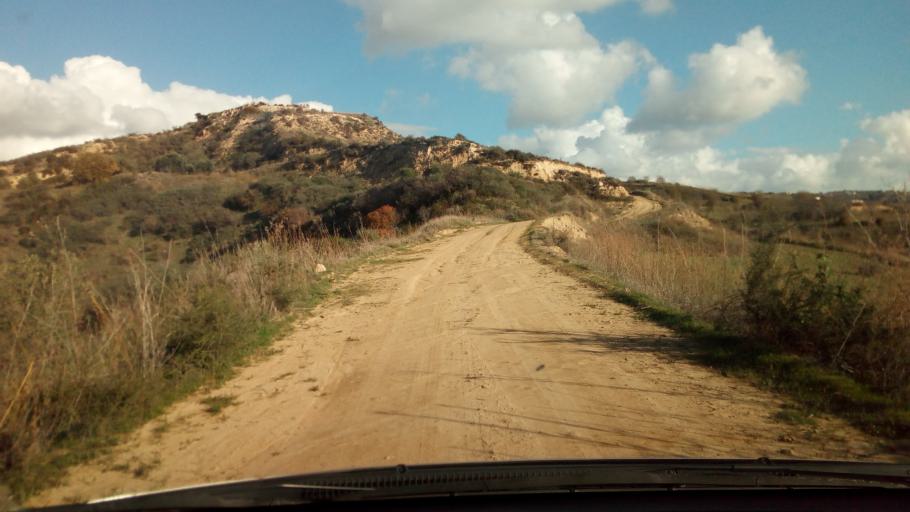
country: CY
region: Pafos
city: Polis
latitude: 34.9408
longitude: 32.4903
